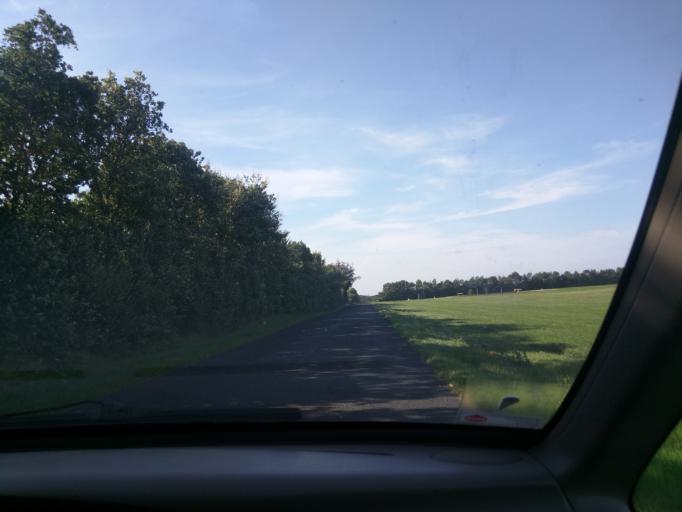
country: DK
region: Central Jutland
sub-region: Viborg Kommune
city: Bjerringbro
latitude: 56.4893
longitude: 9.5935
